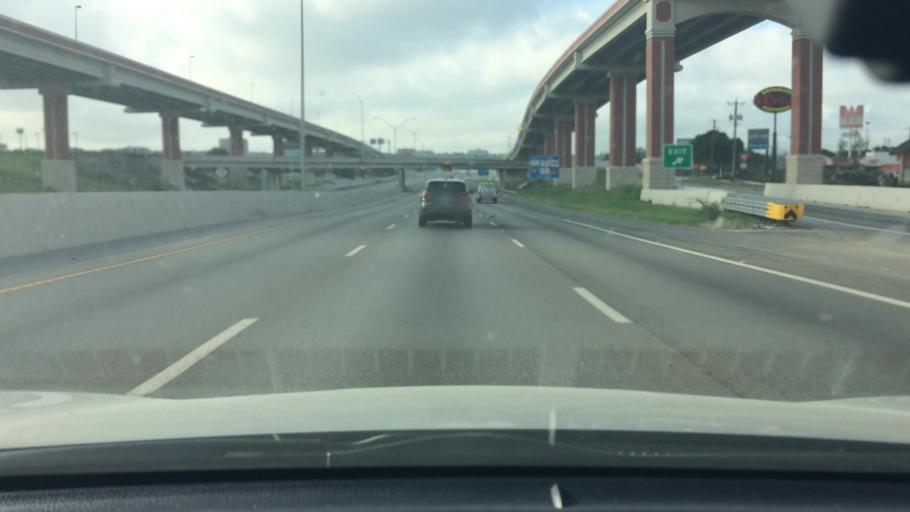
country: US
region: Texas
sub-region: Bexar County
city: Alamo Heights
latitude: 29.5173
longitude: -98.4785
